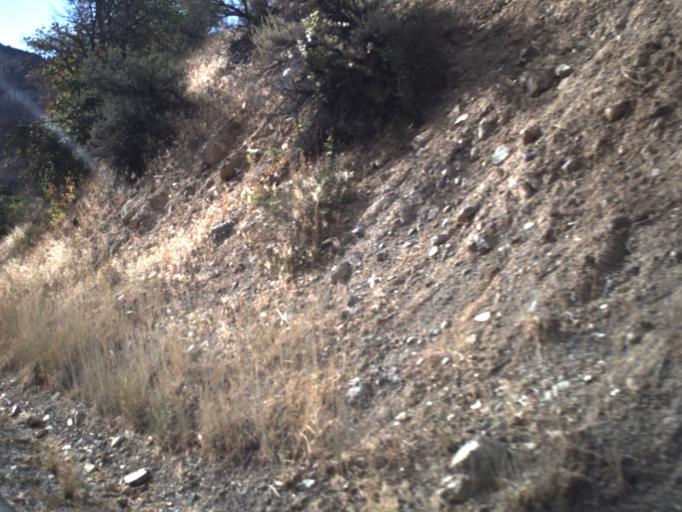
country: US
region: Utah
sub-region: Cache County
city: Millville
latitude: 41.6277
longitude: -111.6905
